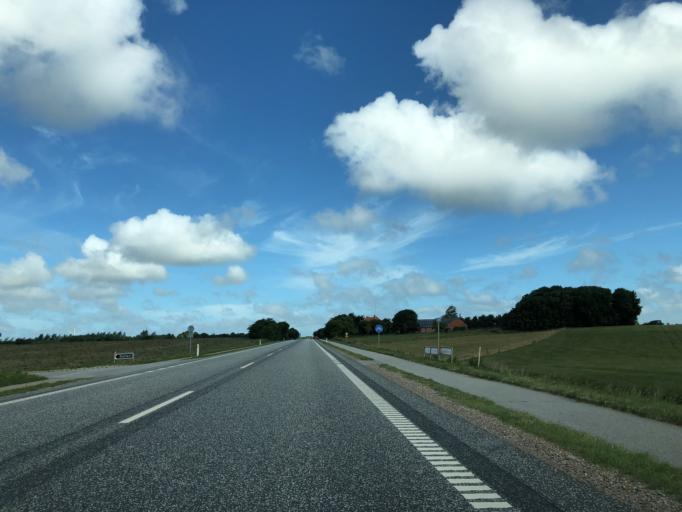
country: DK
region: Central Jutland
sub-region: Struer Kommune
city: Struer
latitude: 56.4642
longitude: 8.5888
